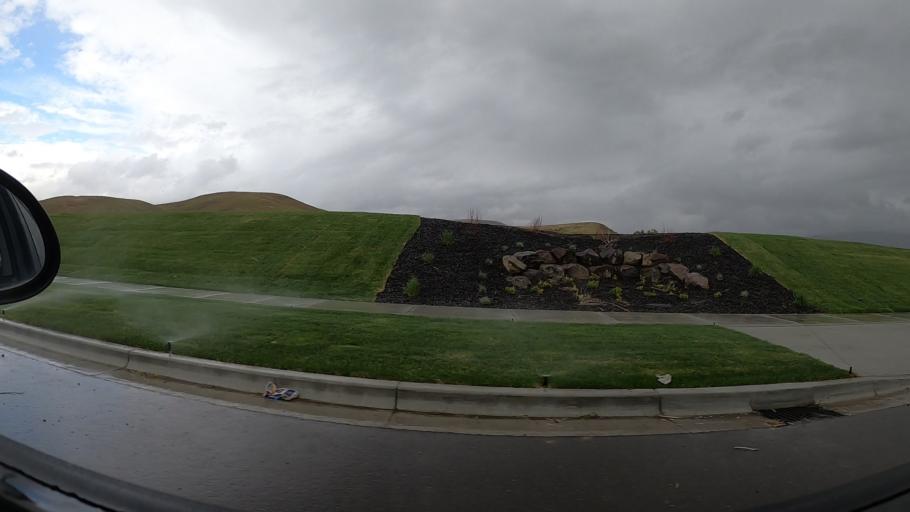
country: US
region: Idaho
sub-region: Ada County
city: Eagle
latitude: 43.7351
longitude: -116.2826
